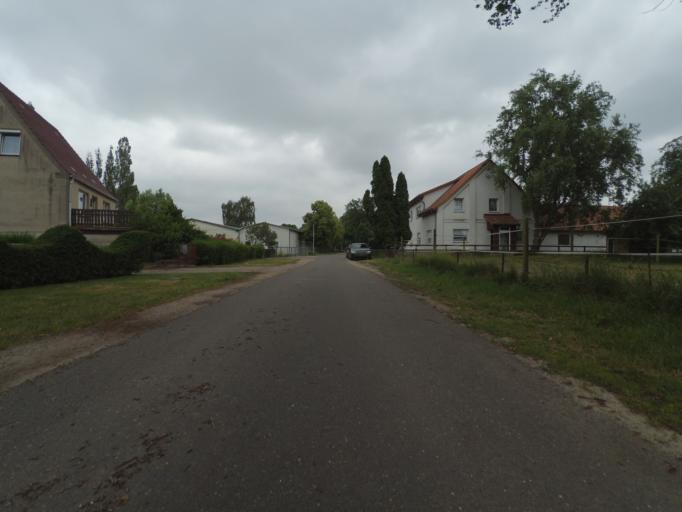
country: DE
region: Mecklenburg-Vorpommern
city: Neustadt-Glewe
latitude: 53.4094
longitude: 11.5749
